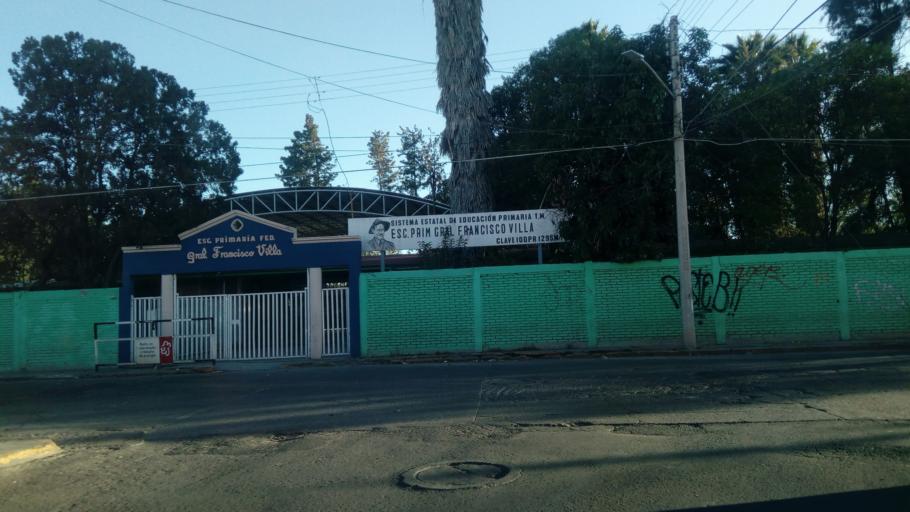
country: MX
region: Durango
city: Victoria de Durango
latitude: 24.0055
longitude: -104.6777
